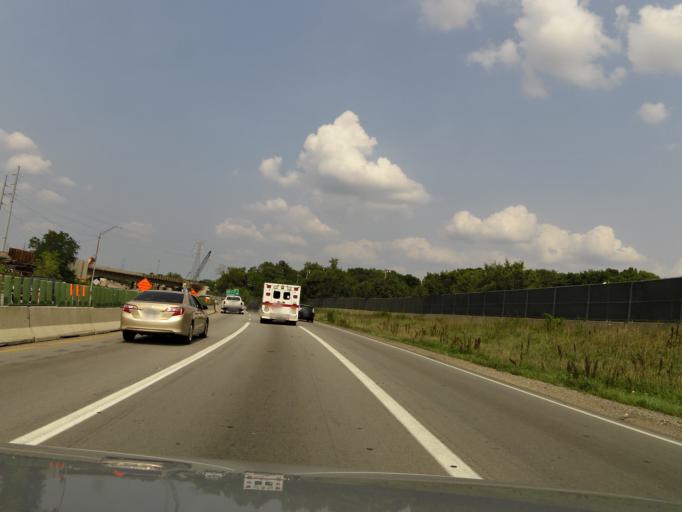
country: US
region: Ohio
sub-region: Hamilton County
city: Saint Bernard
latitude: 39.1718
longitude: -84.4943
